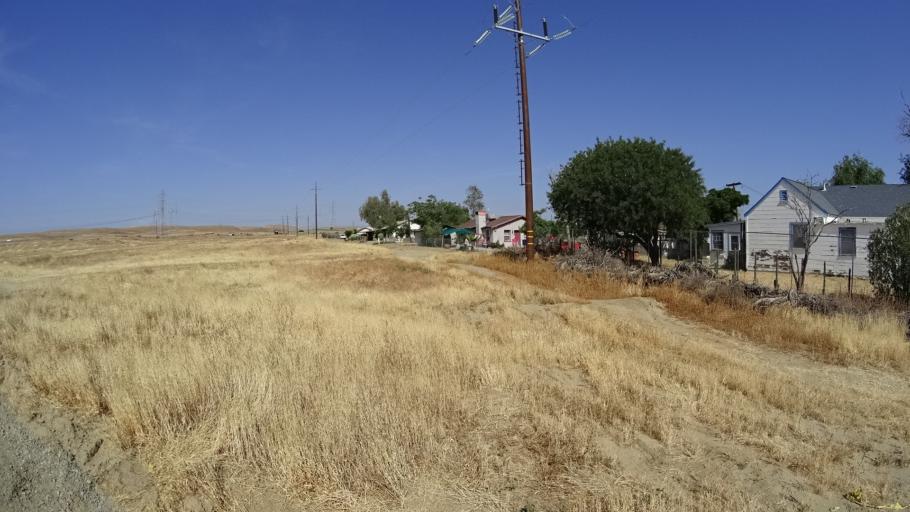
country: US
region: California
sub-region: Kings County
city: Kettleman City
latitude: 36.0071
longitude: -119.9650
